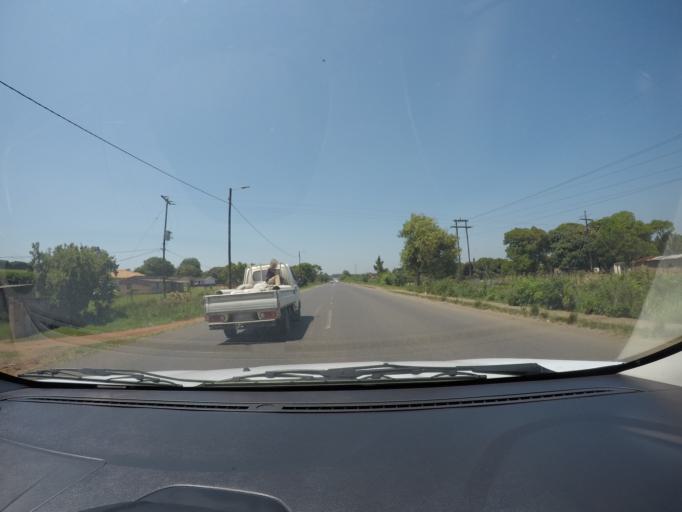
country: ZA
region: KwaZulu-Natal
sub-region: uThungulu District Municipality
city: eSikhawini
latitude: -28.8357
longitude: 31.9378
